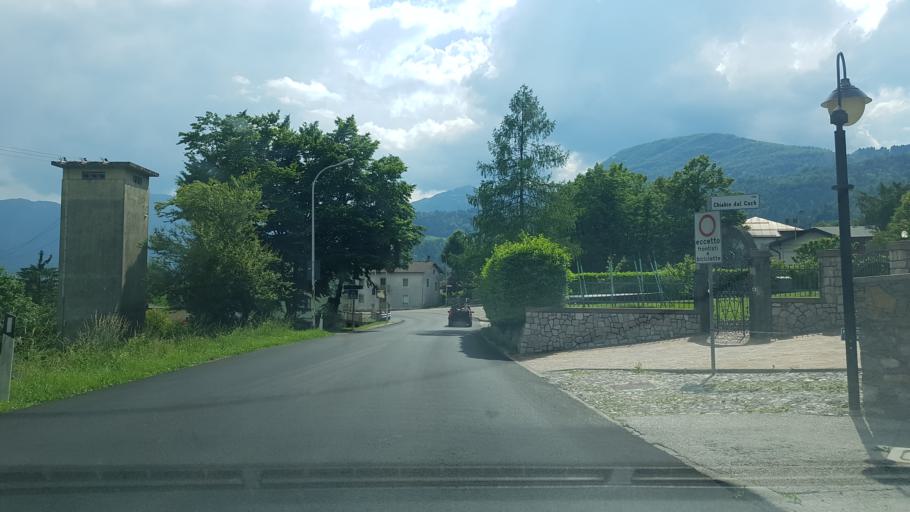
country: IT
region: Friuli Venezia Giulia
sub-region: Provincia di Udine
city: Zuglio
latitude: 46.4329
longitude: 13.0221
